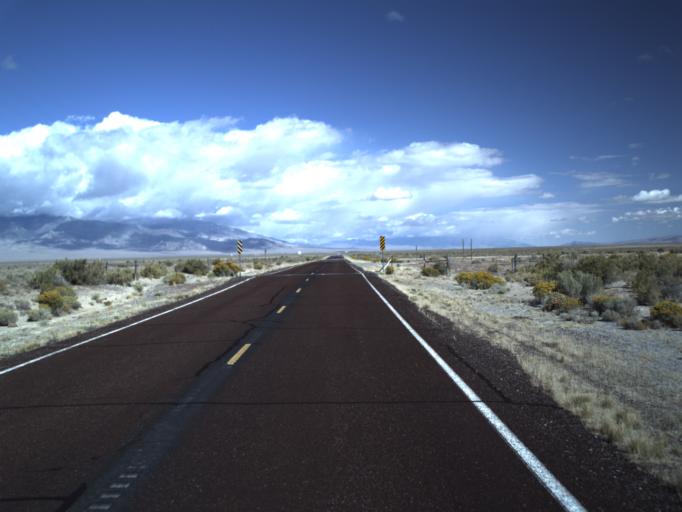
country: US
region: Nevada
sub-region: White Pine County
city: McGill
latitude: 38.9530
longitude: -114.0333
